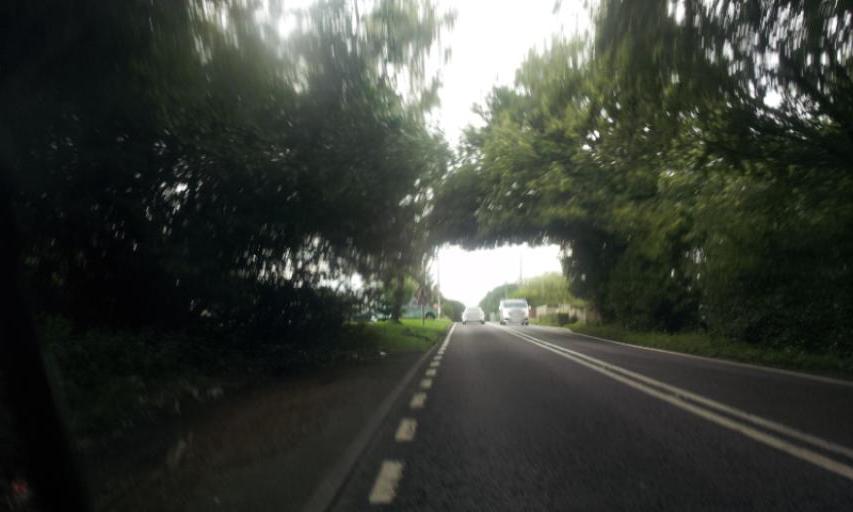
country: GB
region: England
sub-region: Kent
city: Kings Hill
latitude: 51.2661
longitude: 0.3612
